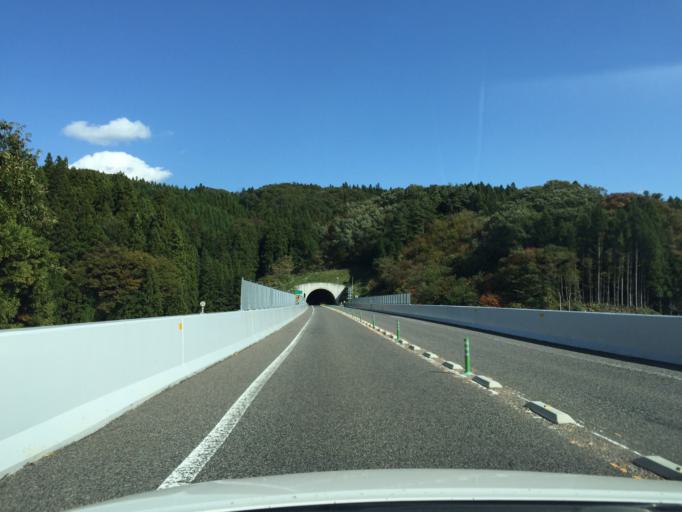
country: JP
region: Fukushima
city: Ishikawa
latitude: 37.2692
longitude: 140.5817
